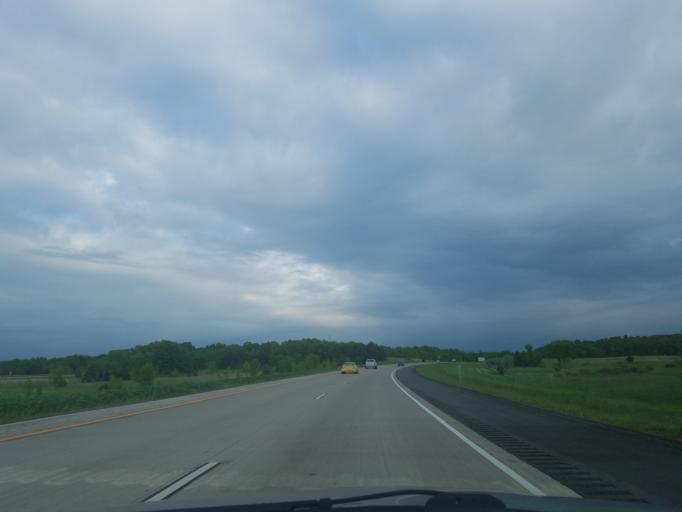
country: US
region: Minnesota
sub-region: Stearns County
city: Collegeville
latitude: 45.5836
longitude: -94.3616
